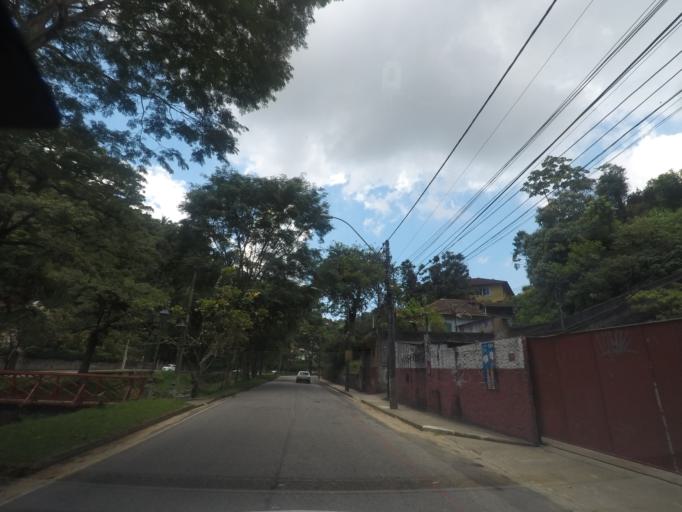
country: BR
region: Rio de Janeiro
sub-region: Petropolis
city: Petropolis
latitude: -22.4979
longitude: -43.1808
